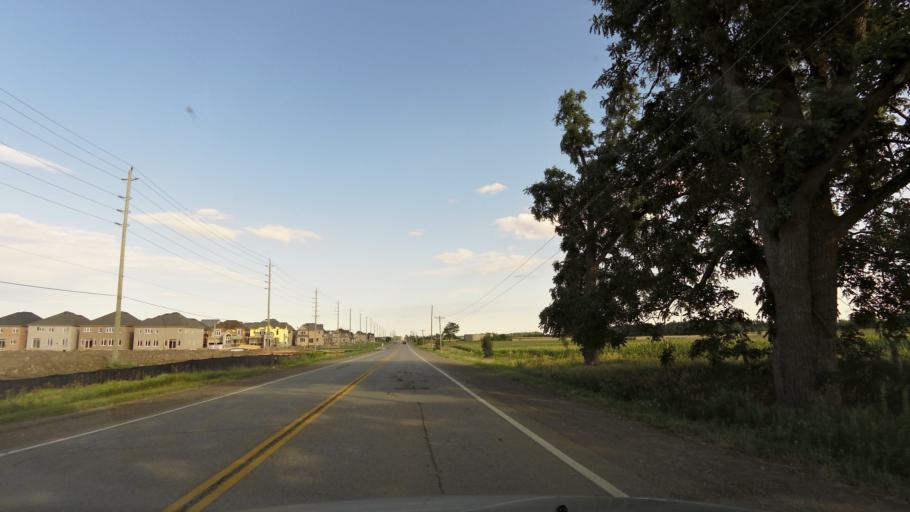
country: CA
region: Ontario
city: Brampton
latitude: 43.6849
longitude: -79.8540
